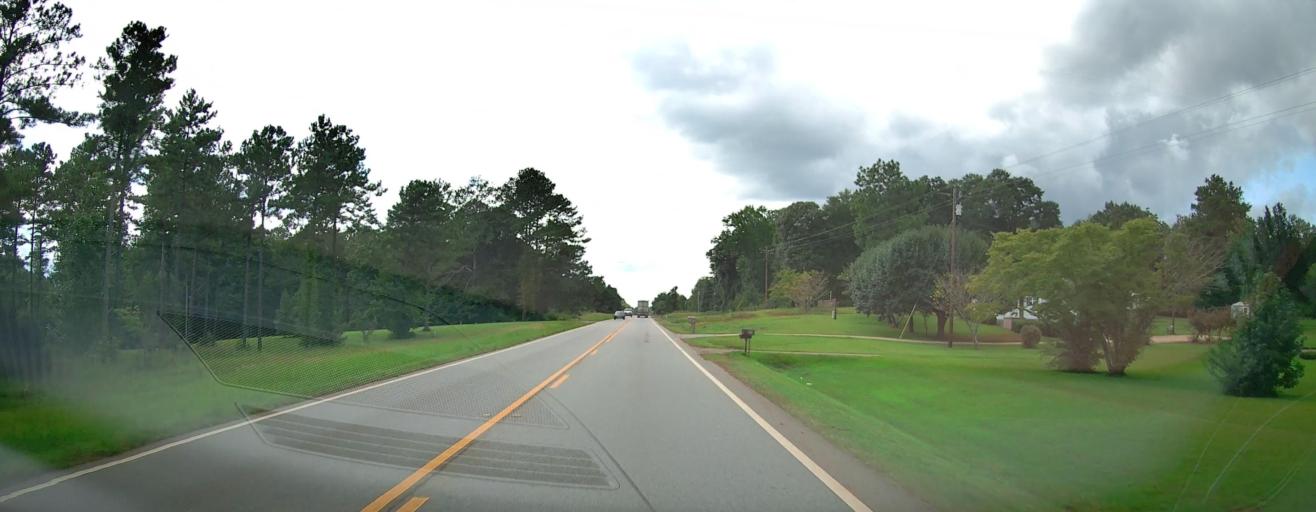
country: US
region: Georgia
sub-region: Bibb County
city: West Point
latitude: 32.8645
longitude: -83.8515
